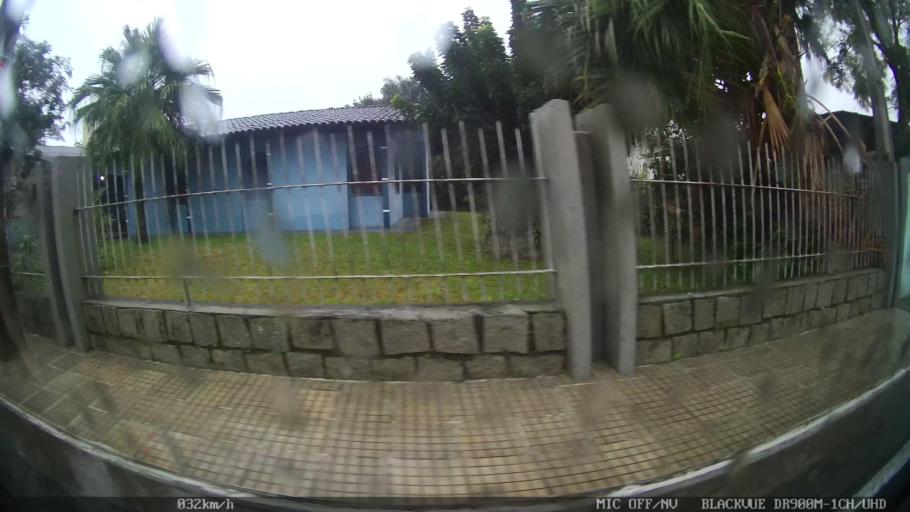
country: BR
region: Santa Catarina
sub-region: Itajai
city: Itajai
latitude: -26.9172
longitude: -48.6838
